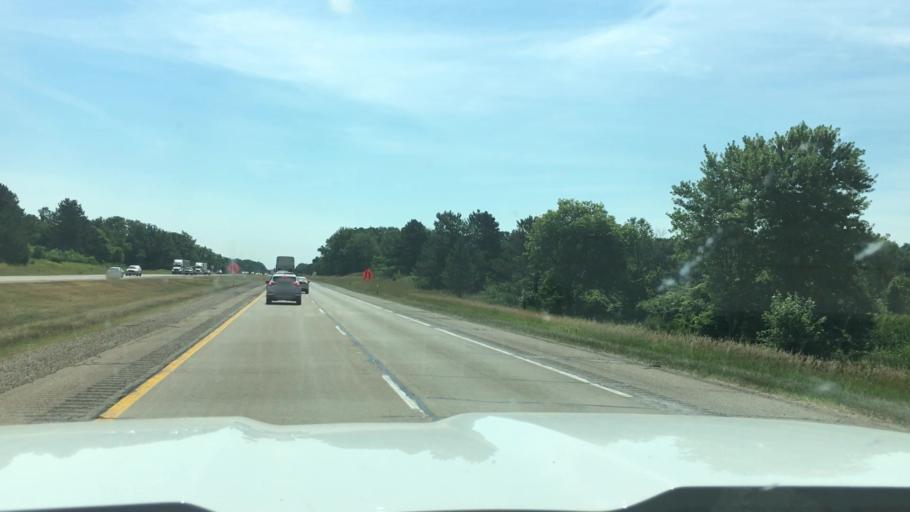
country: US
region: Michigan
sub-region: Ionia County
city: Portland
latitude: 42.8256
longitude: -84.8325
